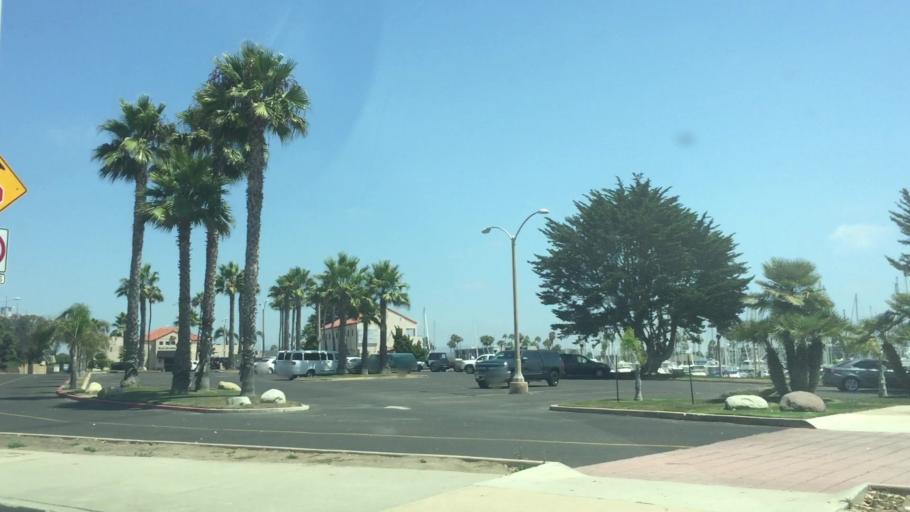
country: US
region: California
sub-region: Ventura County
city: Oxnard Shores
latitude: 34.1755
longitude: -119.2307
